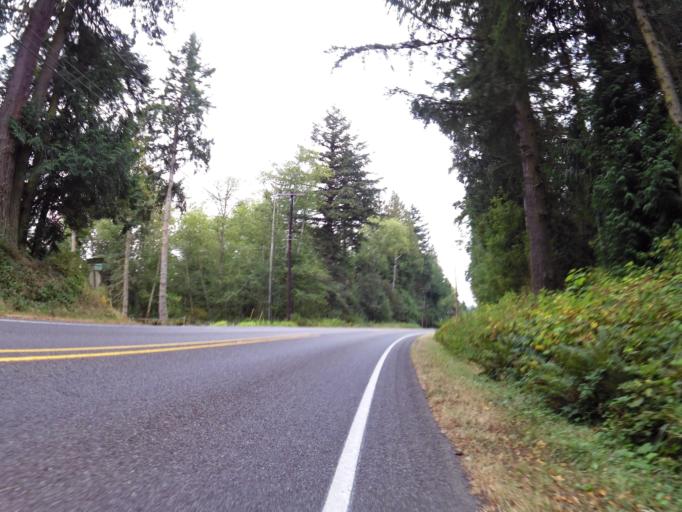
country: US
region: Washington
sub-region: Jefferson County
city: Port Ludlow
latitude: 47.9663
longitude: -122.6977
